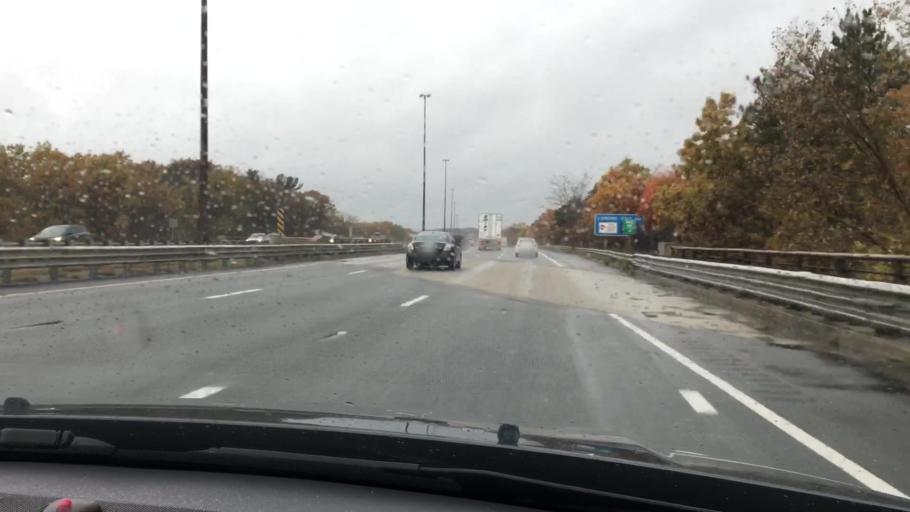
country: US
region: Massachusetts
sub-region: Middlesex County
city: Chelmsford
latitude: 42.6066
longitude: -71.3389
